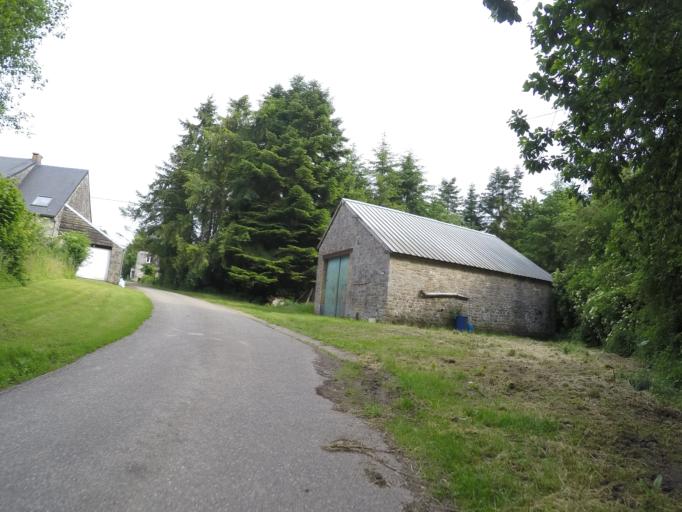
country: BE
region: Wallonia
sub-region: Province de Namur
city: Assesse
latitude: 50.3288
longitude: 5.0480
